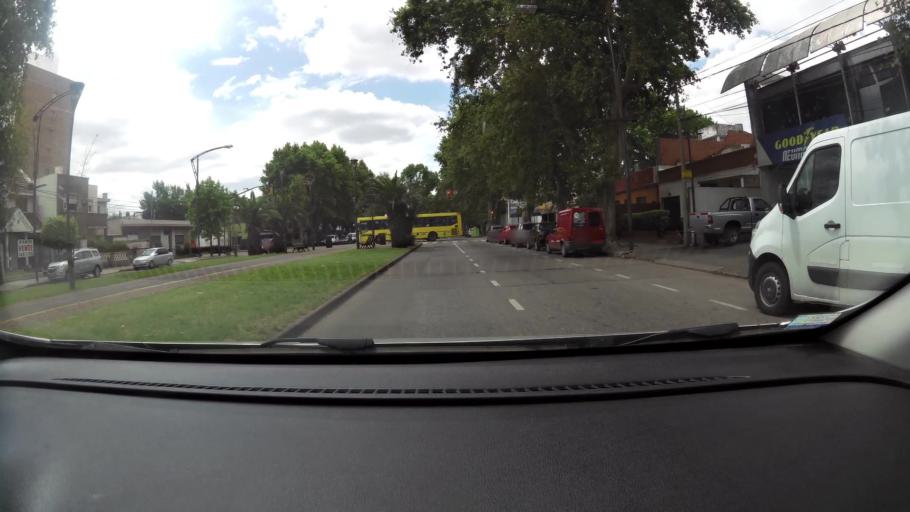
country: AR
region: Santa Fe
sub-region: Departamento de Rosario
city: Rosario
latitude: -32.9689
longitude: -60.6596
